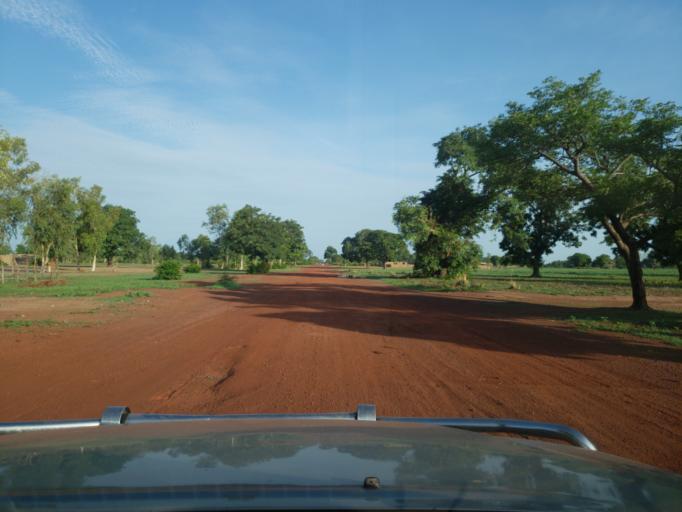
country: ML
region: Sikasso
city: Koutiala
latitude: 12.4165
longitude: -5.5713
